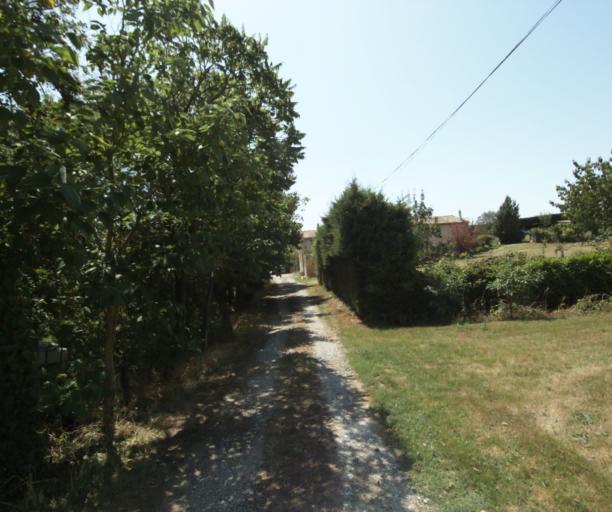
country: FR
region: Midi-Pyrenees
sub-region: Departement de la Haute-Garonne
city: Auriac-sur-Vendinelle
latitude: 43.4610
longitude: 1.8261
